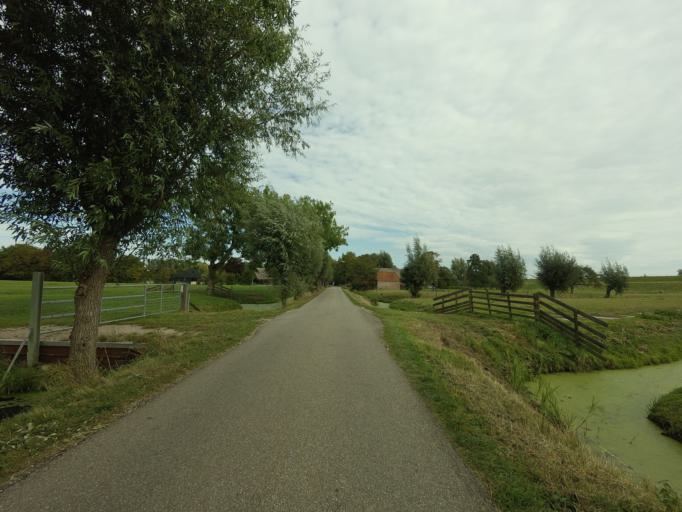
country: NL
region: South Holland
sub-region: Gemeente Schoonhoven
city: Schoonhoven
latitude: 51.9424
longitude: 4.8767
